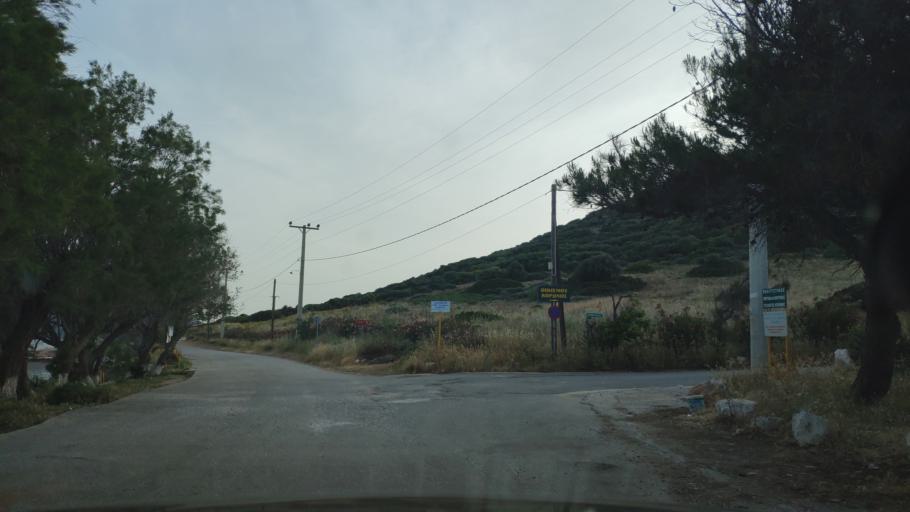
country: GR
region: Attica
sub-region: Nomarchia Anatolikis Attikis
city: Limin Mesoyaias
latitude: 37.8714
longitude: 24.0354
